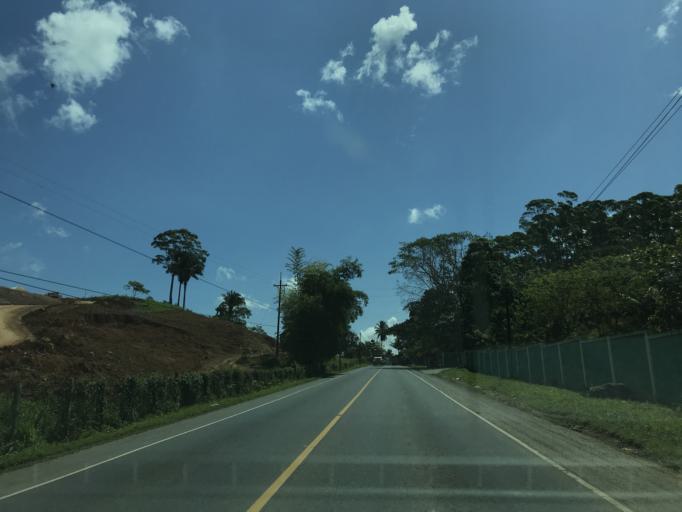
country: GT
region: Izabal
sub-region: Municipio de Puerto Barrios
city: Puerto Barrios
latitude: 15.6629
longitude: -88.5527
